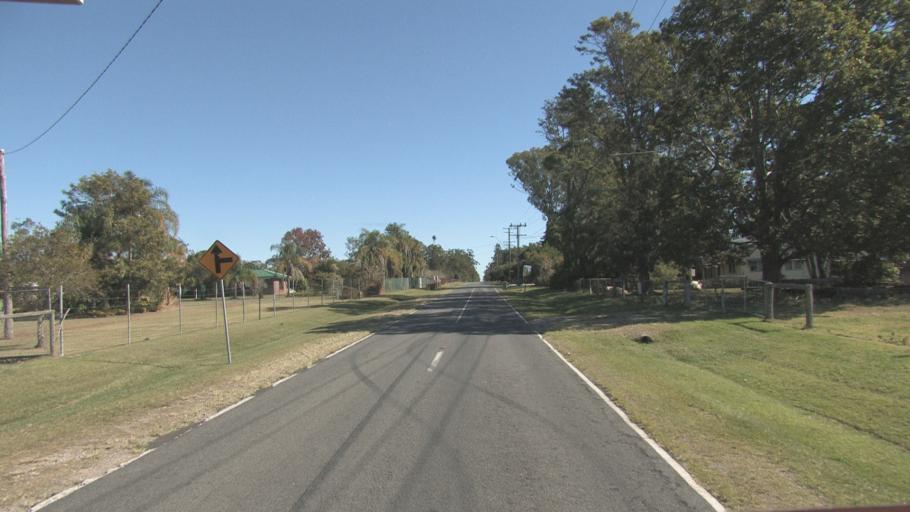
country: AU
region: Queensland
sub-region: Logan
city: Park Ridge South
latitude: -27.7190
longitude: 153.0583
